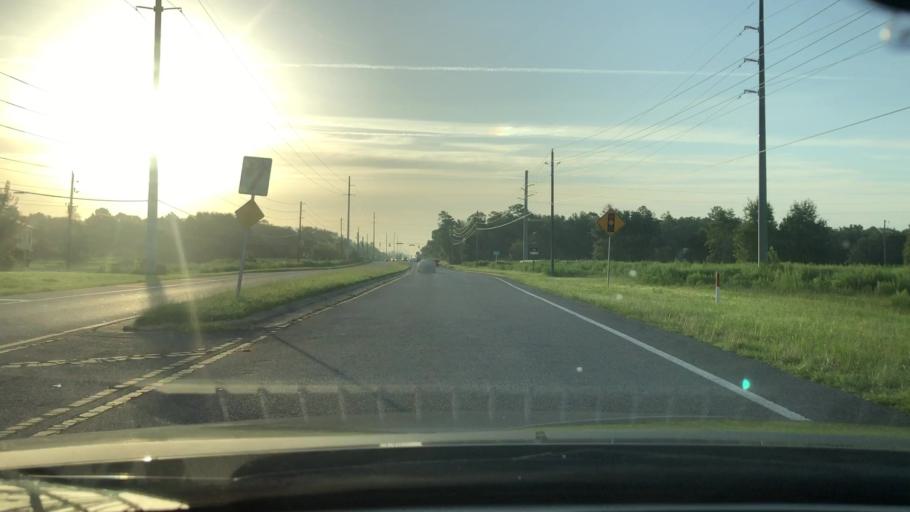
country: US
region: Florida
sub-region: Marion County
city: Belleview
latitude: 29.0260
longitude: -82.2004
